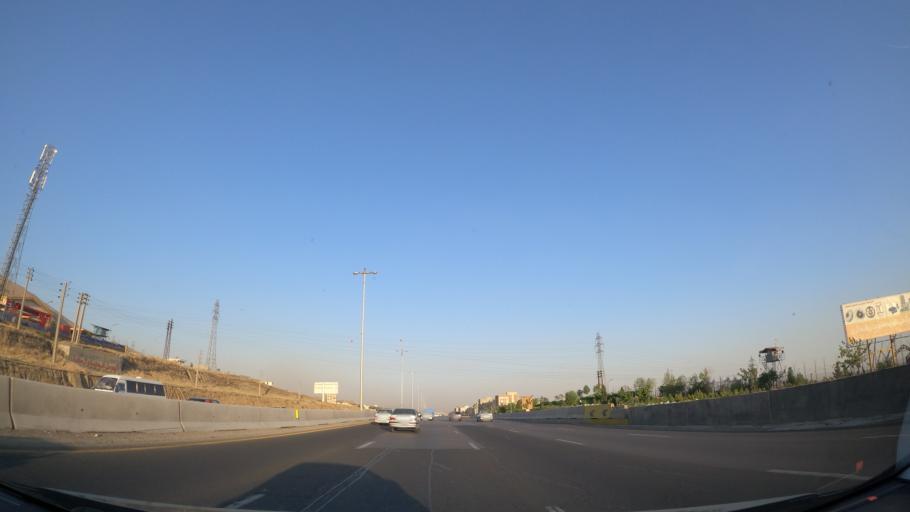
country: IR
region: Tehran
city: Shahr-e Qods
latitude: 35.7611
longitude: 51.0632
